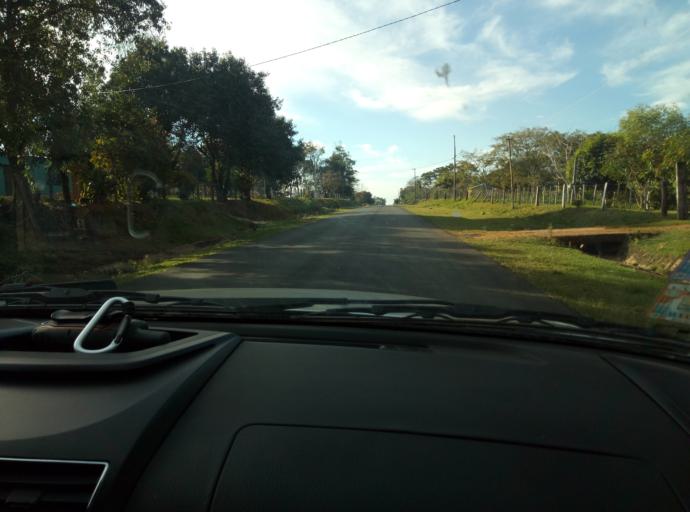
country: PY
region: Caaguazu
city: Carayao
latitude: -25.1618
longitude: -56.3123
